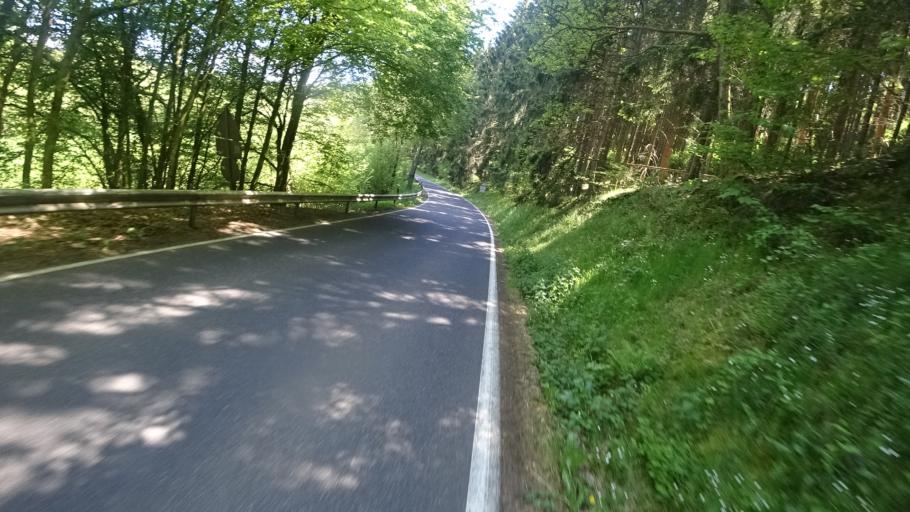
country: DE
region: Rheinland-Pfalz
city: Elben
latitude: 50.7472
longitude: 7.8379
